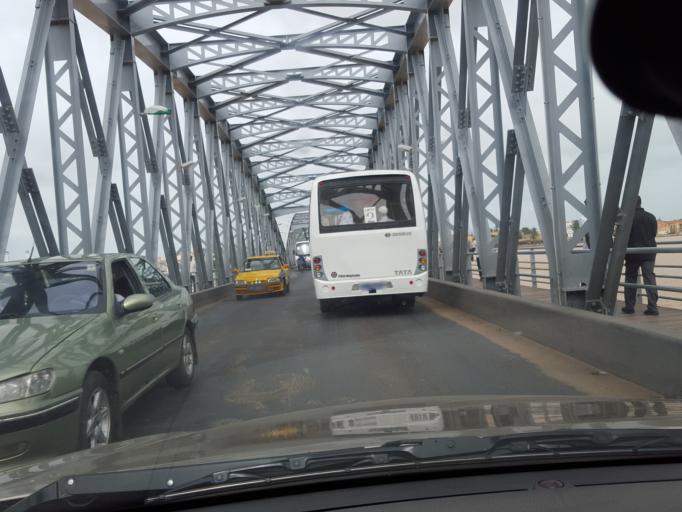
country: SN
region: Saint-Louis
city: Saint-Louis
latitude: 16.0257
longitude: -16.4988
